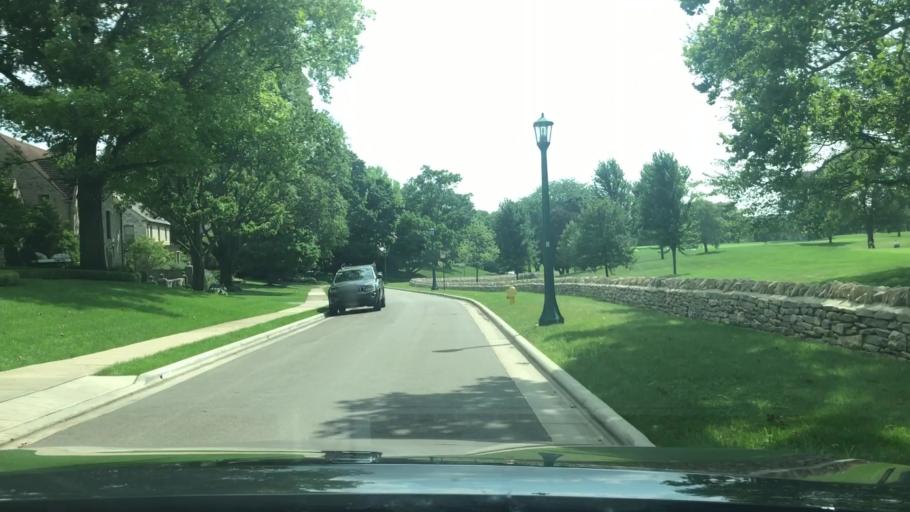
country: US
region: Ohio
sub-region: Franklin County
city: Upper Arlington
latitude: 40.0013
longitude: -83.0698
